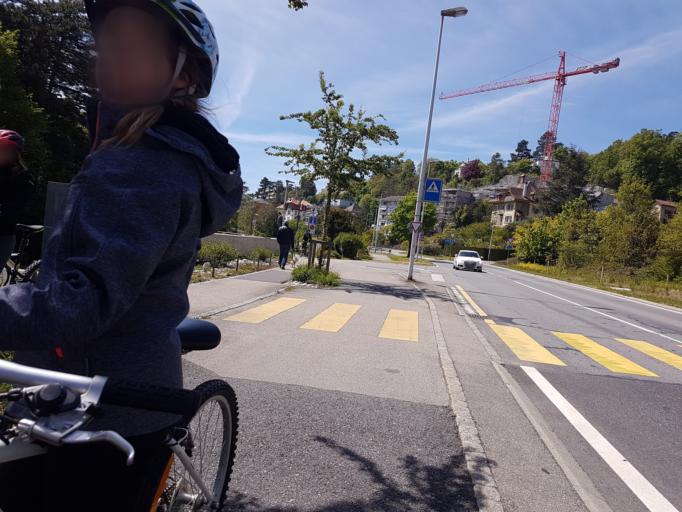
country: CH
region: Neuchatel
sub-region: Neuchatel District
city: Saint-Blaise
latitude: 47.0024
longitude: 6.9587
